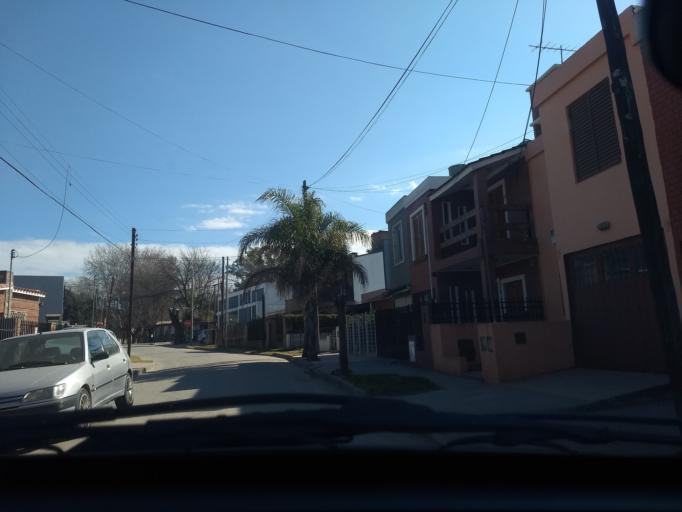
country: AR
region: Cordoba
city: Salsipuedes
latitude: -31.1394
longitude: -64.2960
